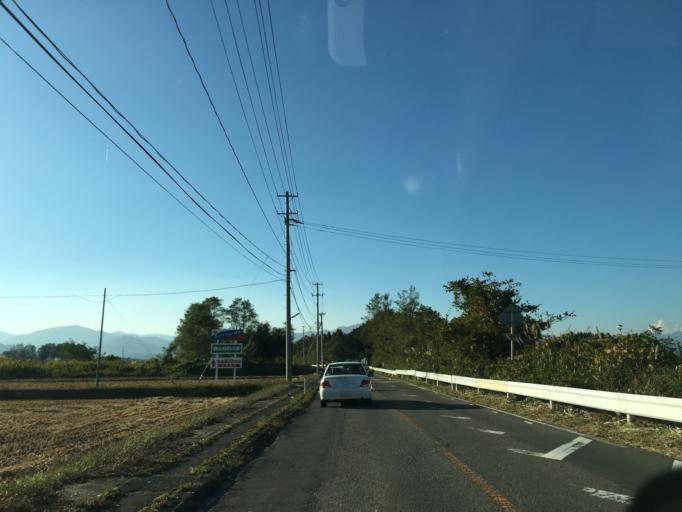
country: JP
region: Fukushima
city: Koriyama
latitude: 37.3906
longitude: 140.2971
